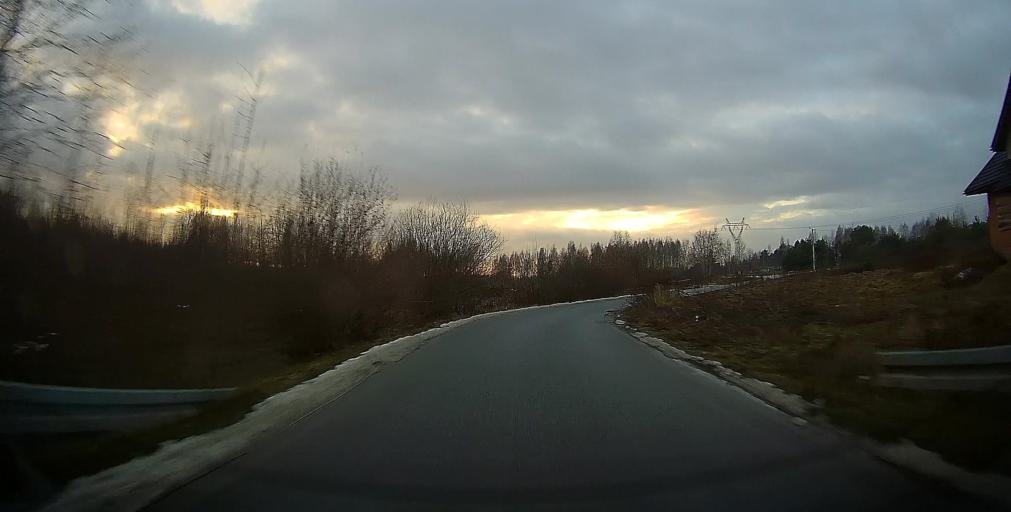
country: PL
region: Masovian Voivodeship
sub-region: Radom
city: Radom
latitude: 51.4542
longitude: 21.1256
